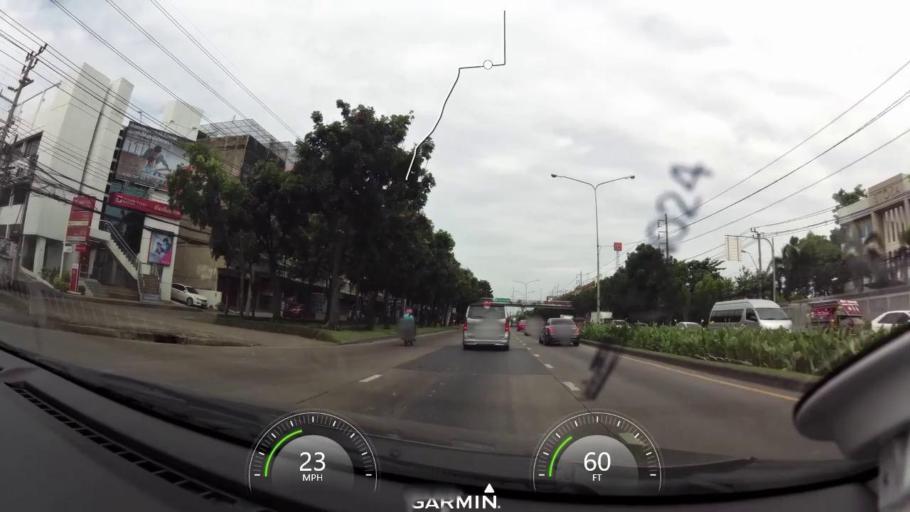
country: TH
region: Bangkok
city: Nong Khaem
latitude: 13.7062
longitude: 100.3526
